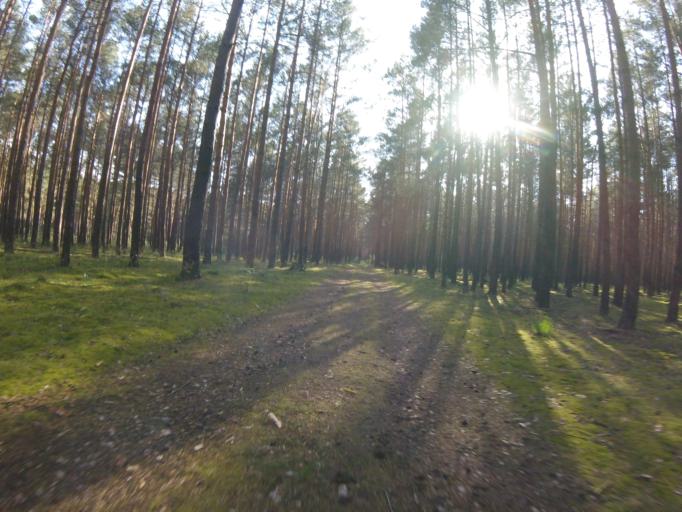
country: DE
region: Brandenburg
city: Halbe
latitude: 52.1114
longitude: 13.7311
